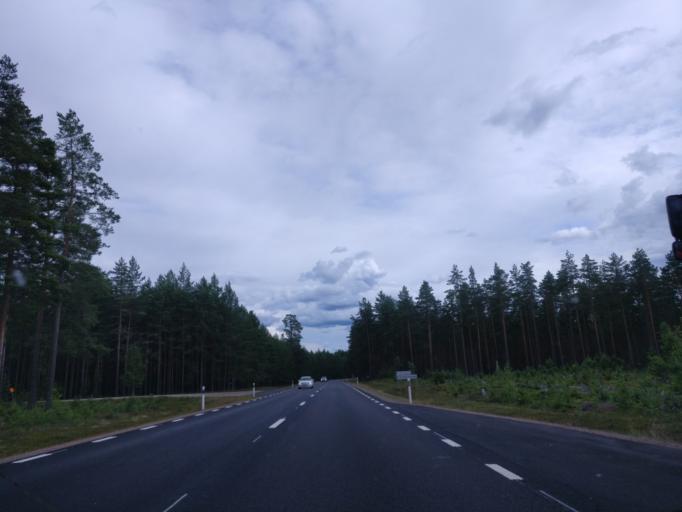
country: SE
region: Vaermland
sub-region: Hagfors Kommun
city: Hagfors
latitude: 60.0444
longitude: 13.5803
